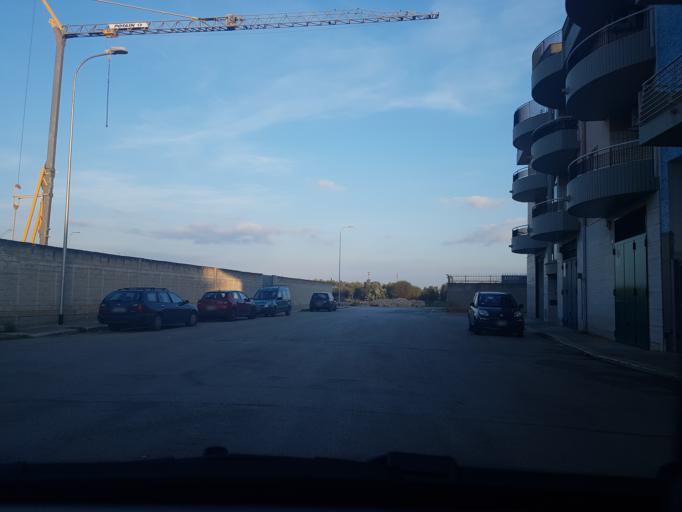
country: IT
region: Apulia
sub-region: Provincia di Bari
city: Bitritto
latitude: 41.0385
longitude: 16.8298
